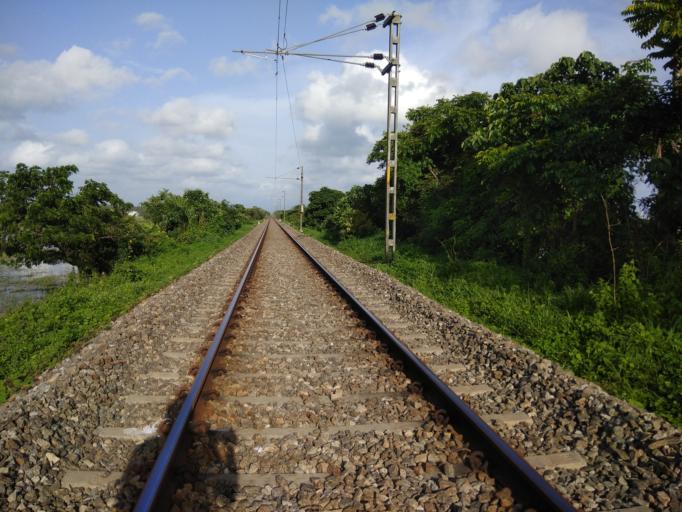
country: IN
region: Kerala
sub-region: Thrissur District
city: Avanoor
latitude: 10.5595
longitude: 76.1791
